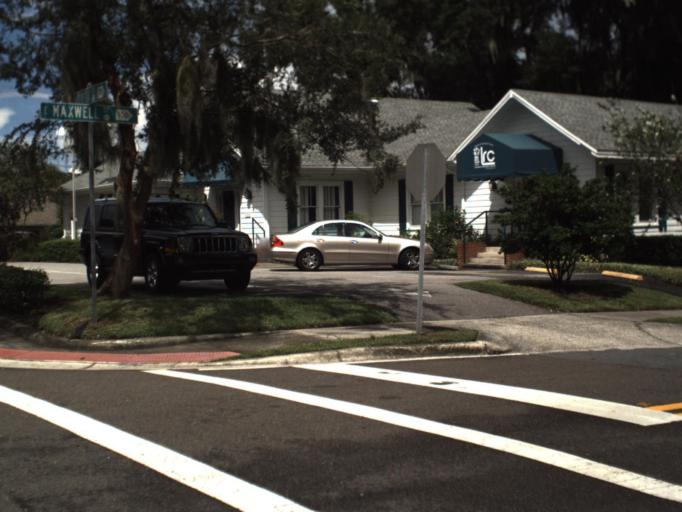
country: US
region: Florida
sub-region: Polk County
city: Lakeland
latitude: 28.0227
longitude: -81.9570
